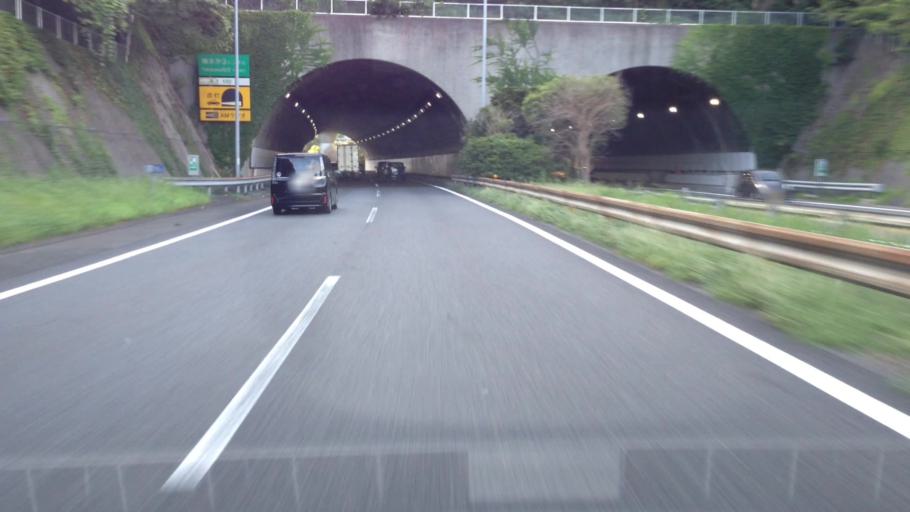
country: JP
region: Kanagawa
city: Zushi
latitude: 35.3224
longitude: 139.6028
